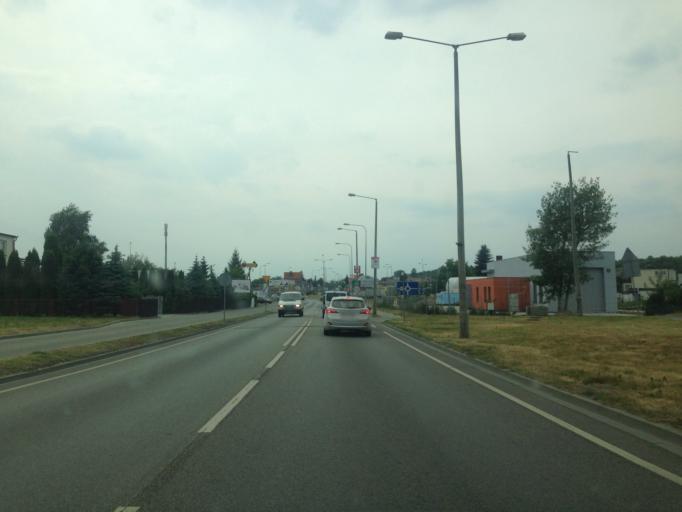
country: PL
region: Kujawsko-Pomorskie
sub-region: Grudziadz
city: Grudziadz
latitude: 53.5039
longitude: 18.8022
